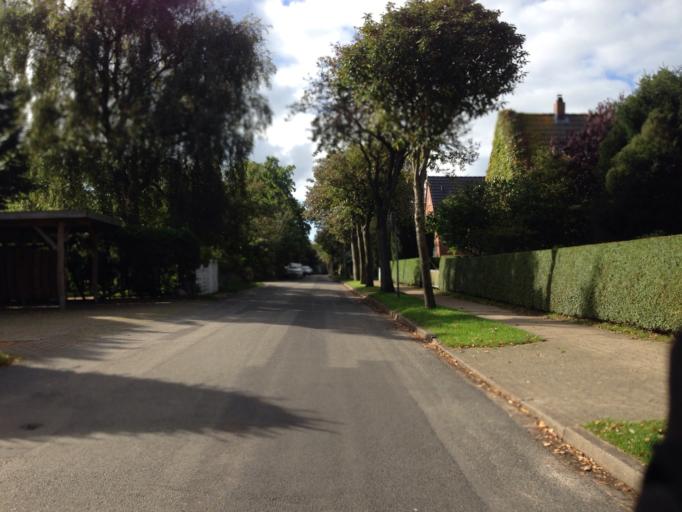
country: DE
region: Schleswig-Holstein
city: Wyk auf Fohr
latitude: 54.6859
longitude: 8.5666
